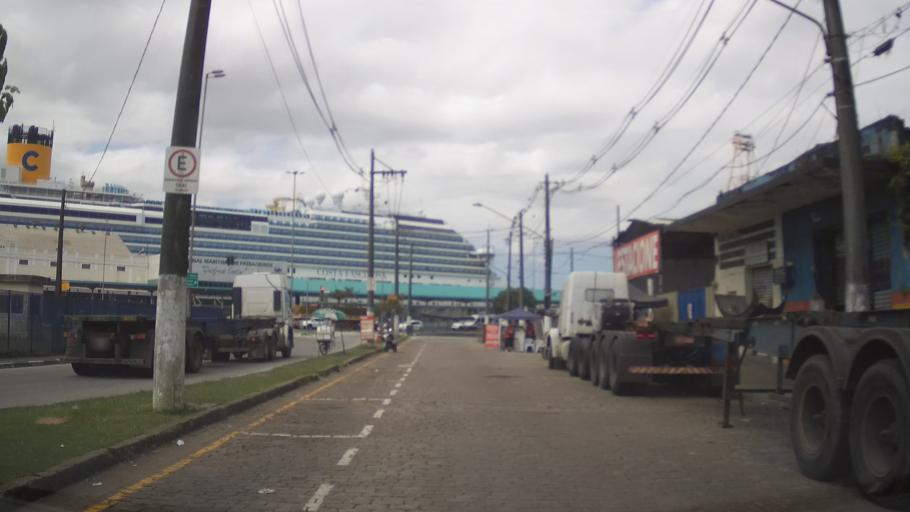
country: BR
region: Sao Paulo
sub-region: Santos
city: Santos
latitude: -23.9513
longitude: -46.3125
